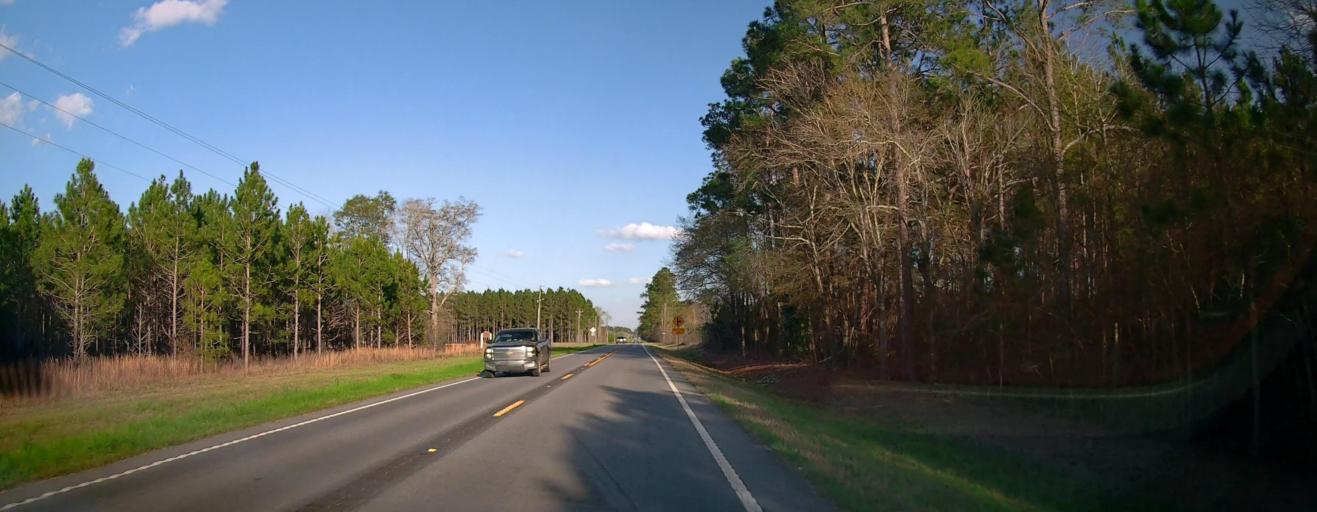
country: US
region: Georgia
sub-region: Evans County
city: Claxton
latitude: 32.1499
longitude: -82.0089
